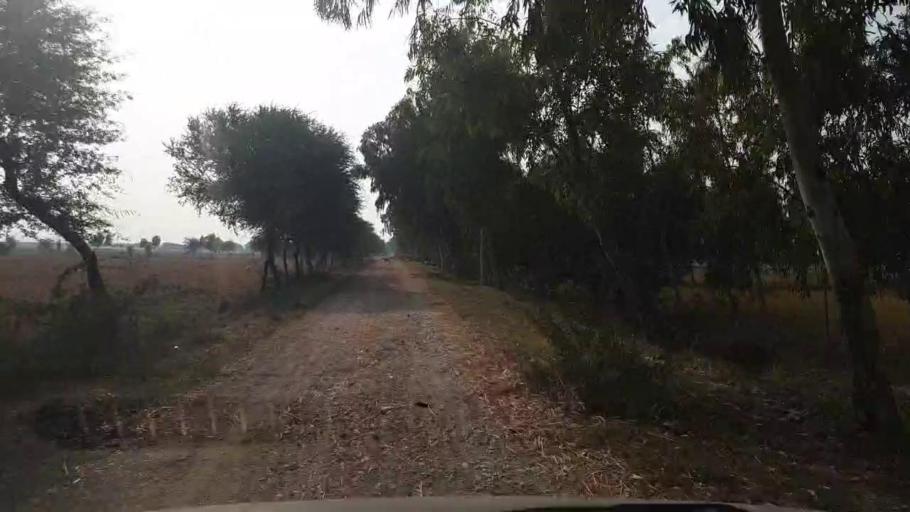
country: PK
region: Sindh
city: Tando Muhammad Khan
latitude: 25.0966
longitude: 68.5035
